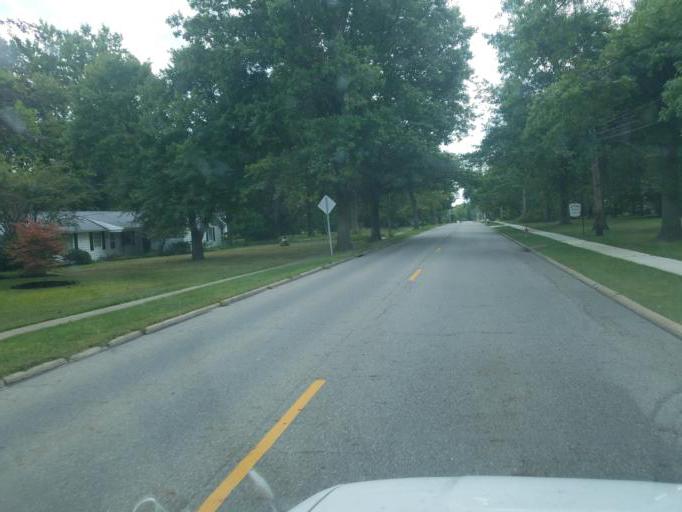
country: US
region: Ohio
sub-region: Portage County
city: Hiram
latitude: 41.3076
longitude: -81.1437
